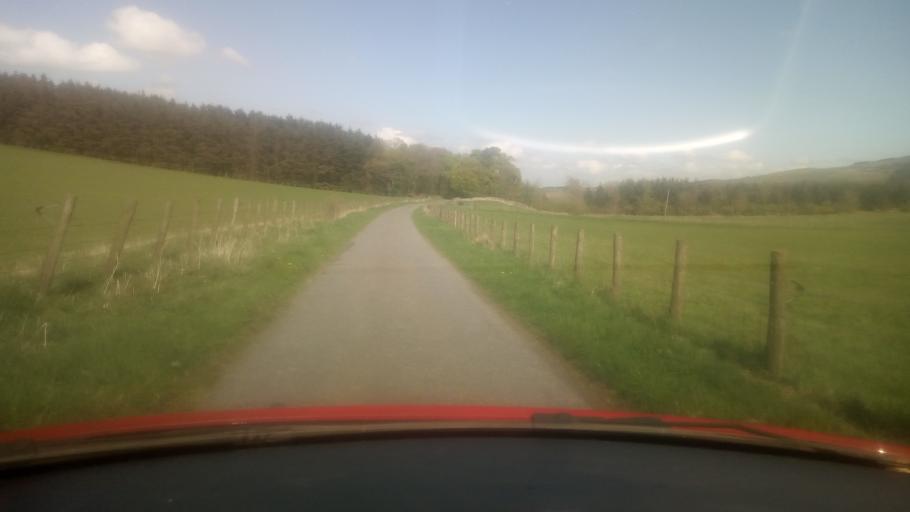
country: GB
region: Scotland
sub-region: The Scottish Borders
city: Hawick
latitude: 55.4244
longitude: -2.7091
